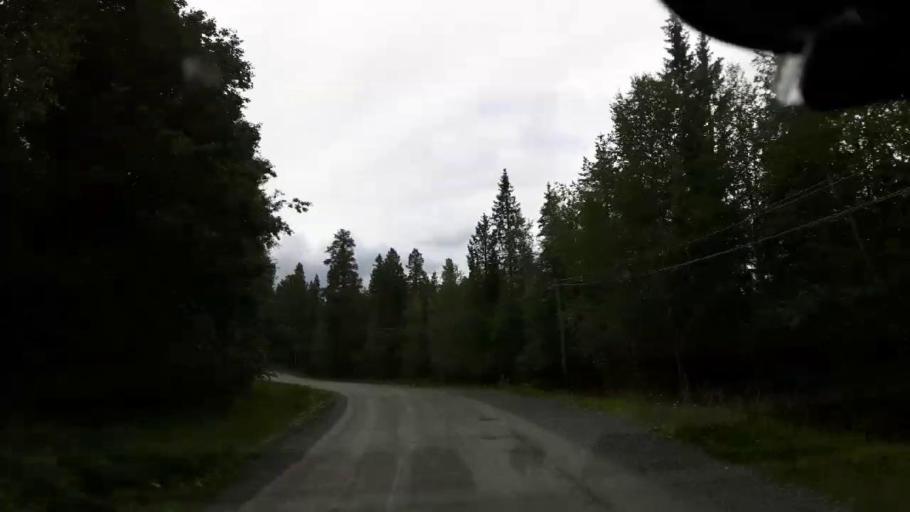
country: SE
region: Jaemtland
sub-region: Krokoms Kommun
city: Valla
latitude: 63.6924
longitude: 13.8668
